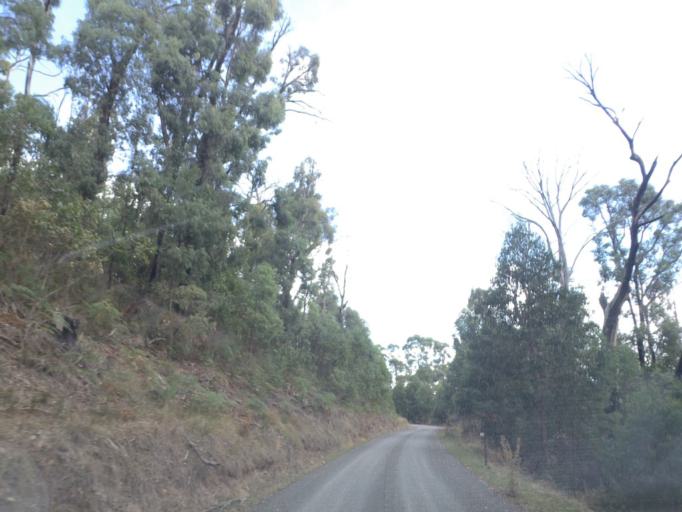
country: AU
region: Victoria
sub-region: Murrindindi
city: Alexandra
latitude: -37.4281
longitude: 145.7597
